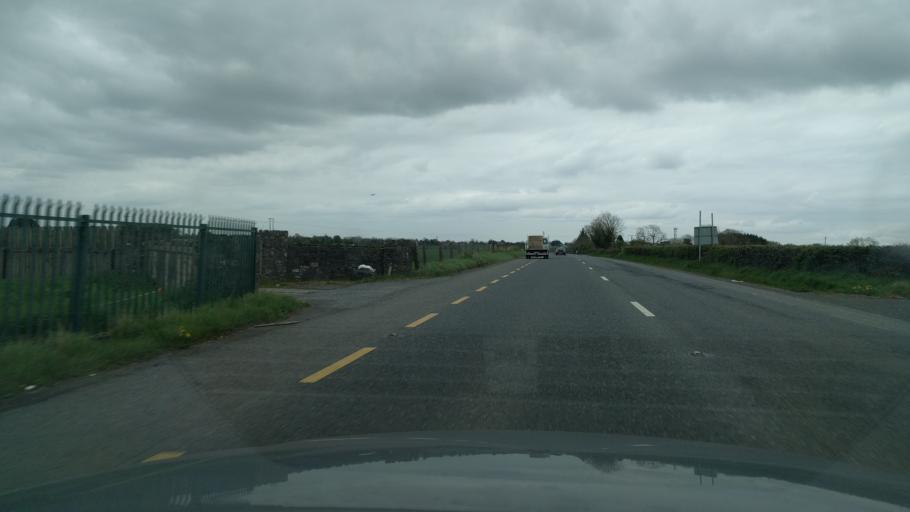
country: IE
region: Leinster
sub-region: Fingal County
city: Blanchardstown
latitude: 53.4561
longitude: -6.3486
